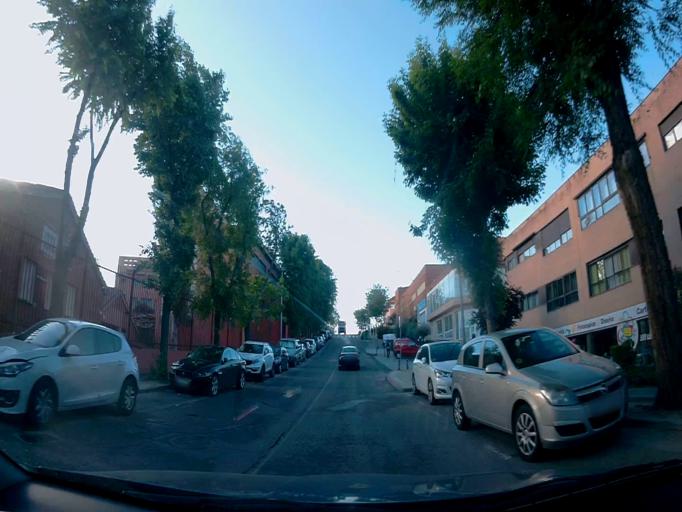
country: ES
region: Madrid
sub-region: Provincia de Madrid
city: San Sebastian de los Reyes
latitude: 40.5582
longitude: -3.6258
